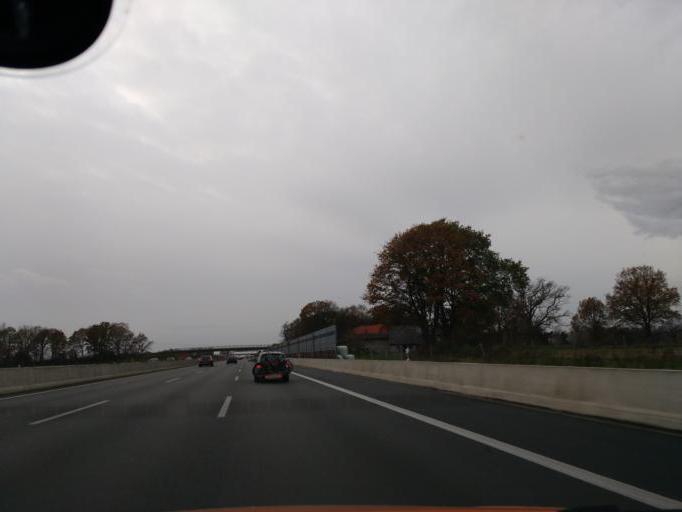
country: DE
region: Lower Saxony
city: Oyten
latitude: 53.0561
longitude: 9.0691
